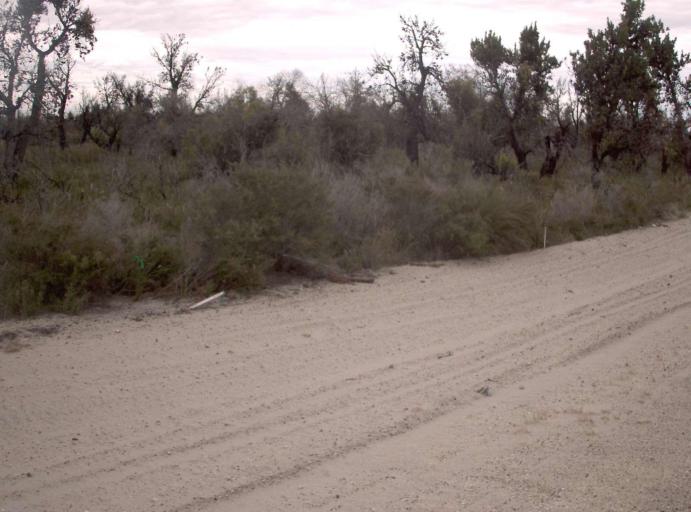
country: AU
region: Victoria
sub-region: East Gippsland
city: Bairnsdale
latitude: -38.1179
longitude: 147.4593
